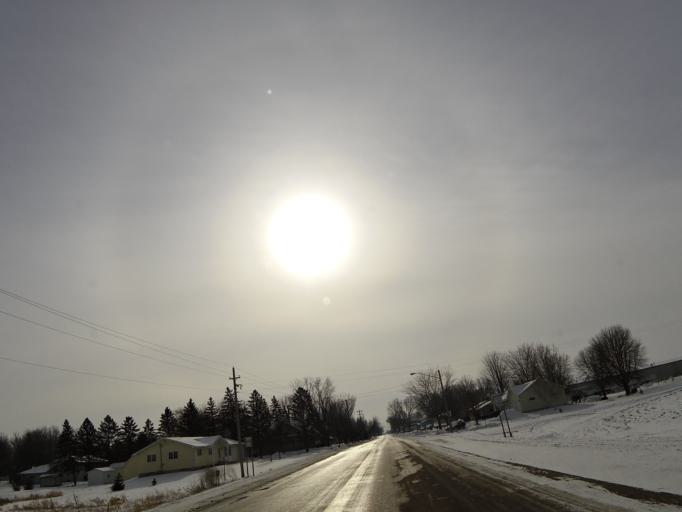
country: US
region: Minnesota
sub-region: McLeod County
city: Lester Prairie
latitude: 44.8883
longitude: -93.9703
